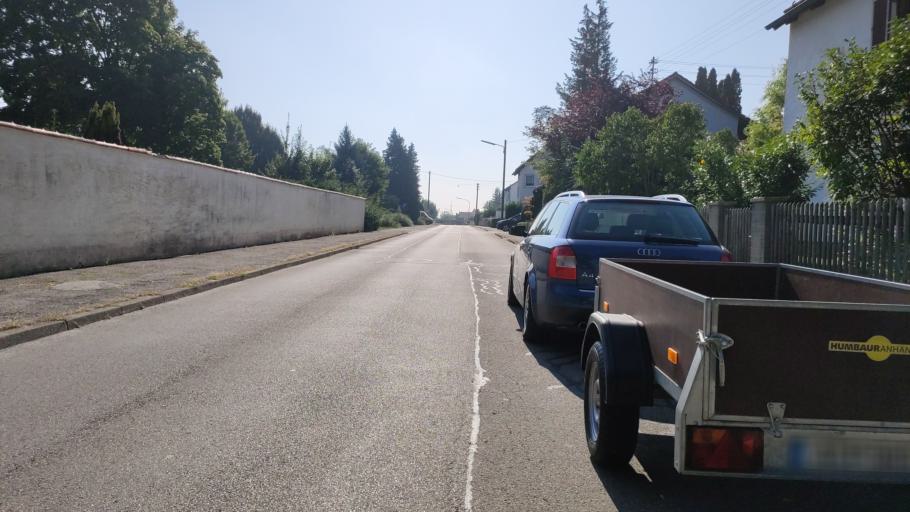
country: DE
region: Bavaria
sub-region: Swabia
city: Bobingen
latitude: 48.2710
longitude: 10.8378
